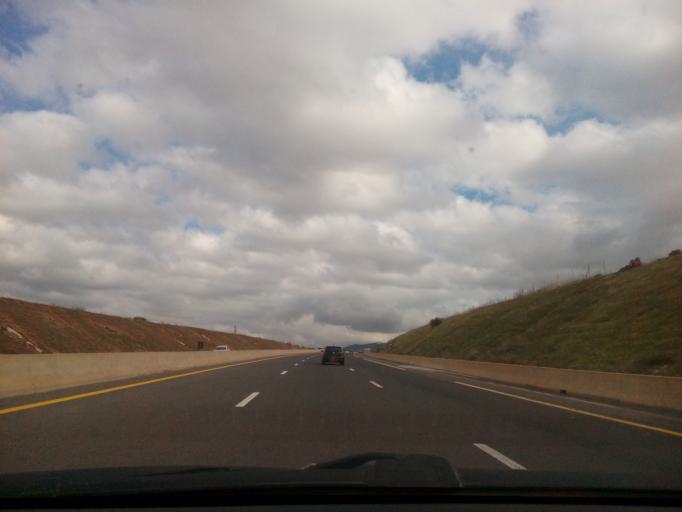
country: DZ
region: Tlemcen
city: Bensekrane
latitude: 34.9862
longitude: -1.2297
